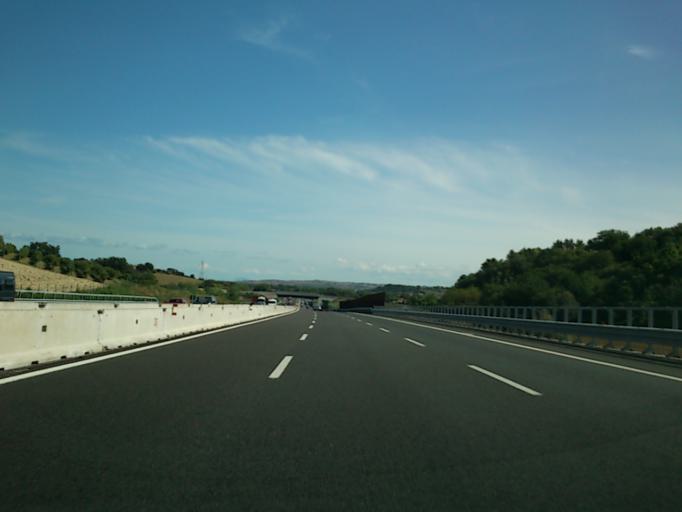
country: IT
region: The Marches
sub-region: Provincia di Pesaro e Urbino
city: Fenile
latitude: 43.8490
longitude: 12.9622
